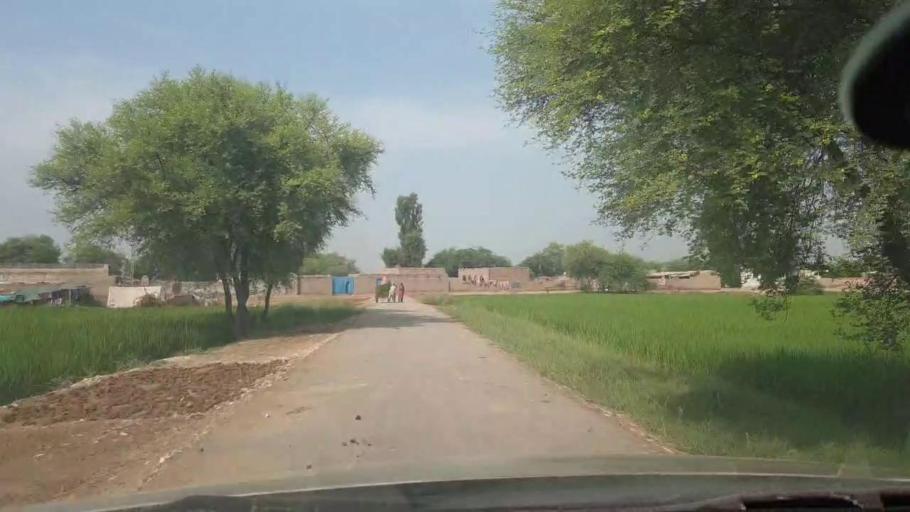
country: PK
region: Sindh
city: Jacobabad
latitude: 28.2953
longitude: 68.4796
